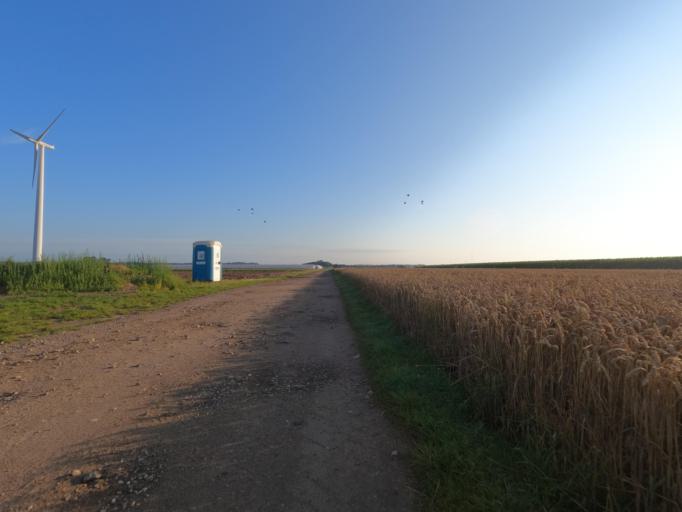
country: DE
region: North Rhine-Westphalia
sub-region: Regierungsbezirk Koln
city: Linnich
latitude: 51.0163
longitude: 6.3101
